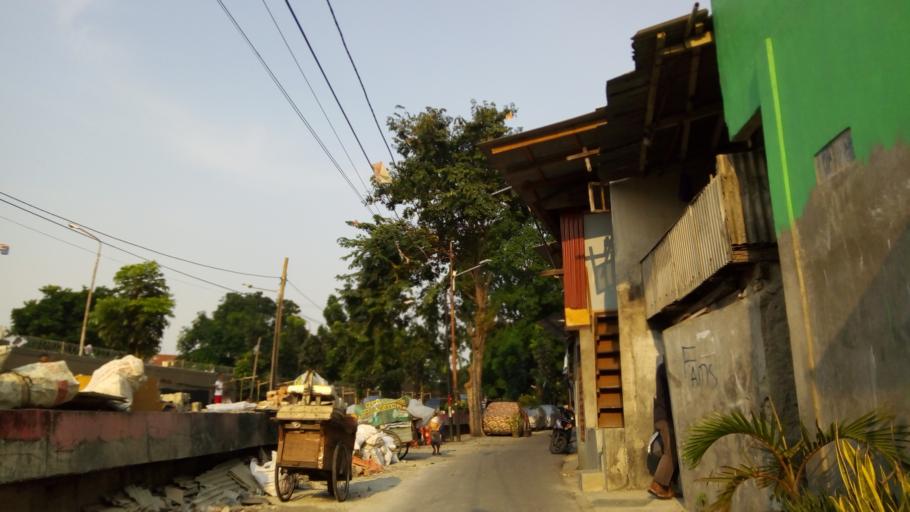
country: ID
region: Jakarta Raya
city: Jakarta
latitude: -6.1963
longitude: 106.8566
